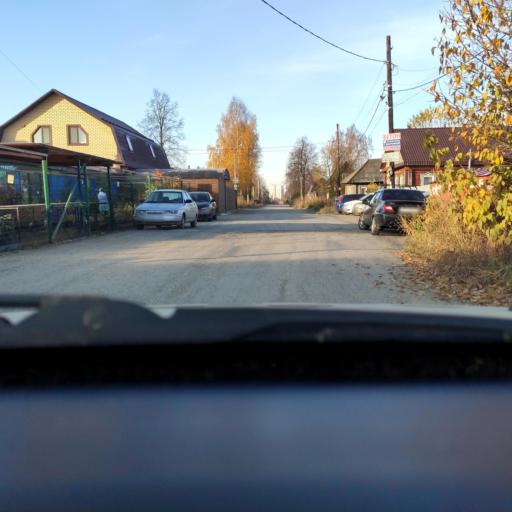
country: RU
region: Perm
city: Perm
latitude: 58.0254
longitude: 56.3319
